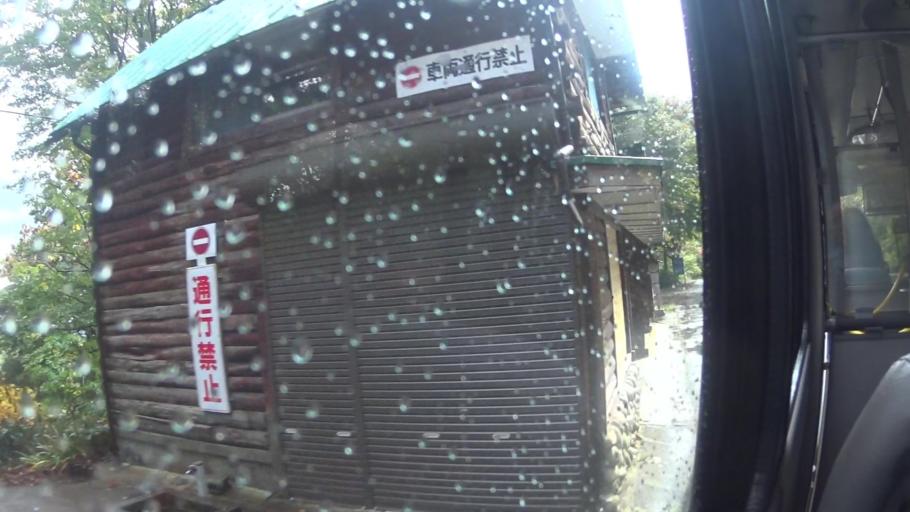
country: JP
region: Kyoto
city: Miyazu
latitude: 35.5919
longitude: 135.1889
